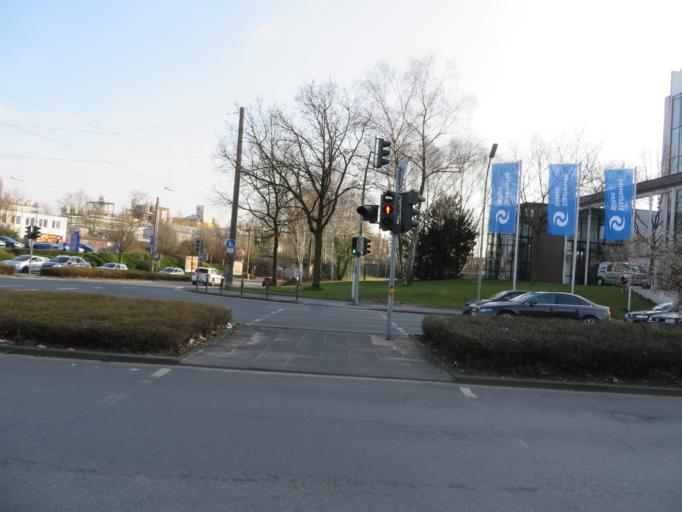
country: DE
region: North Rhine-Westphalia
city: Witten
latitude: 51.4440
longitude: 7.3539
